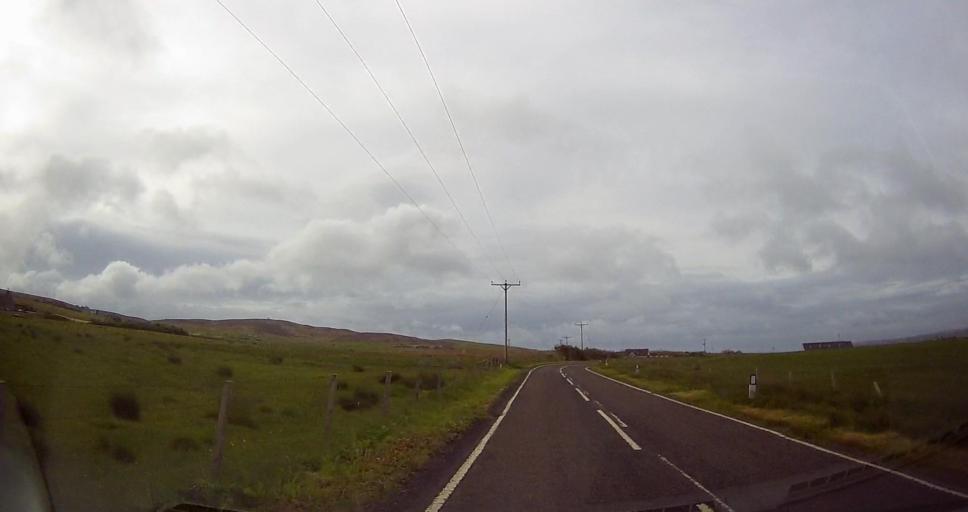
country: GB
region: Scotland
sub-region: Orkney Islands
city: Stromness
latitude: 58.9409
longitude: -3.2138
